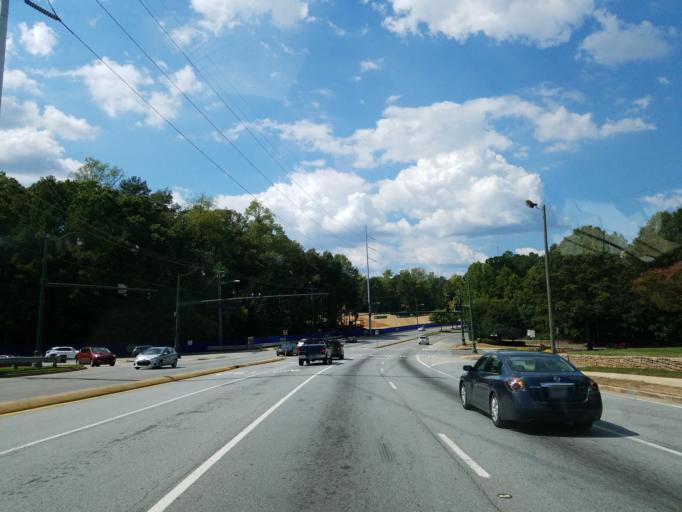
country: US
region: Georgia
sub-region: Fulton County
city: Sandy Springs
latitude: 33.9336
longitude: -84.3610
